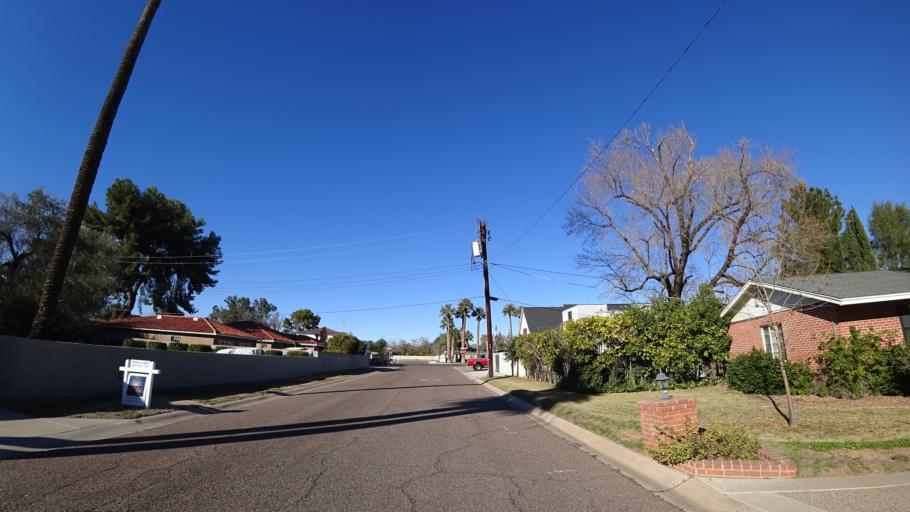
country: US
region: Arizona
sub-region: Maricopa County
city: Phoenix
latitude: 33.5231
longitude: -112.0802
